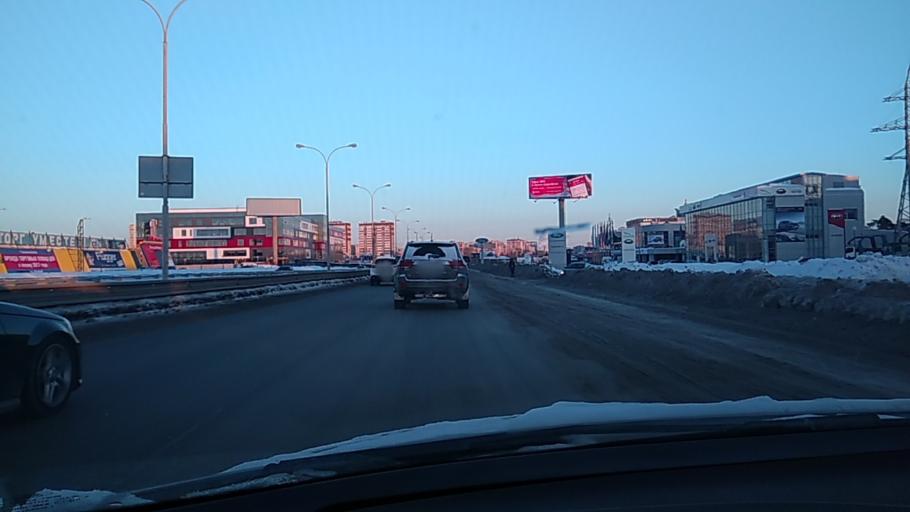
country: RU
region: Sverdlovsk
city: Shirokaya Rechka
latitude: 56.8268
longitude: 60.5173
